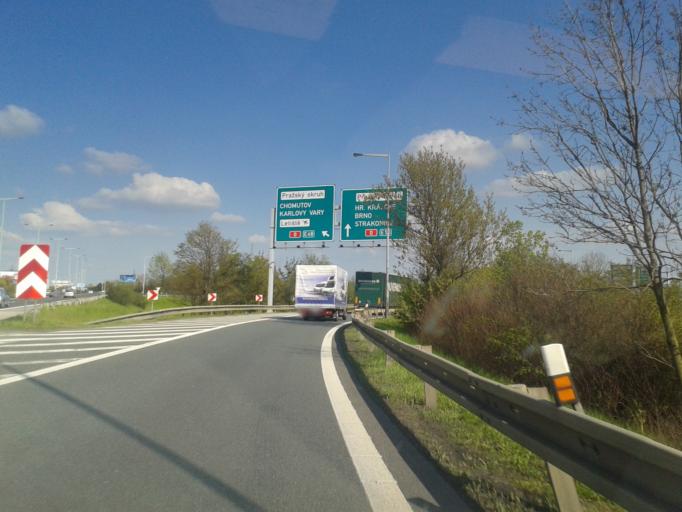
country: CZ
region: Central Bohemia
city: Hostivice
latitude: 50.0488
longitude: 14.2689
